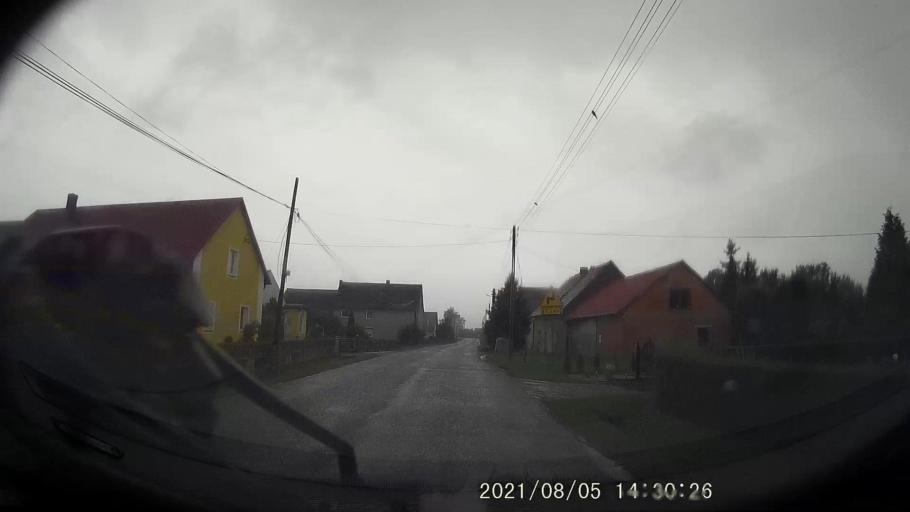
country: PL
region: Opole Voivodeship
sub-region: Powiat nyski
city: Korfantow
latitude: 50.4835
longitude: 17.5557
